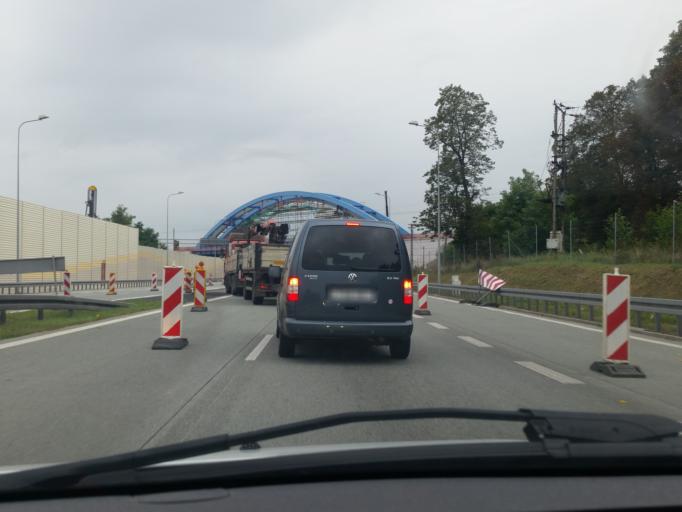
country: PL
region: Lodz Voivodeship
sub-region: Powiat skierniewicki
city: Kowiesy
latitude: 51.9174
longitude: 20.4535
